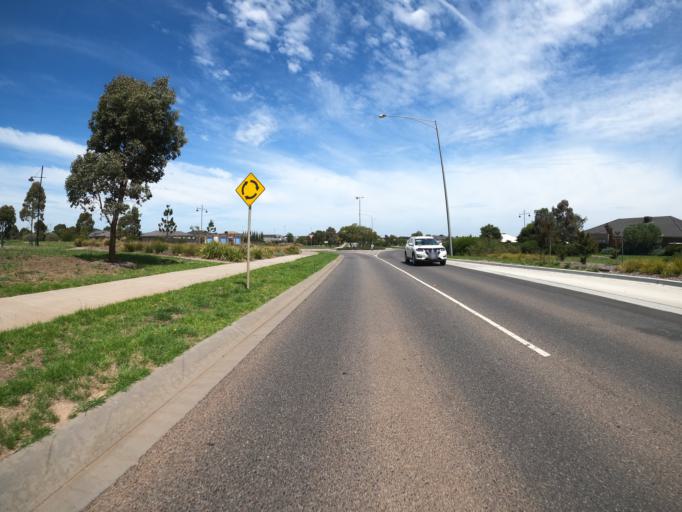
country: AU
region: Victoria
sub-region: Hume
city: Craigieburn
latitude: -37.5704
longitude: 144.9202
